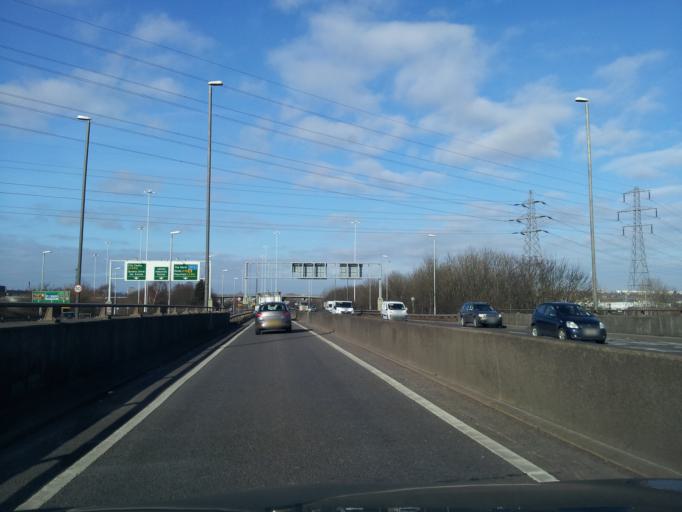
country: GB
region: England
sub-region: Nottingham
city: Nottingham
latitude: 52.9254
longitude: -1.1661
